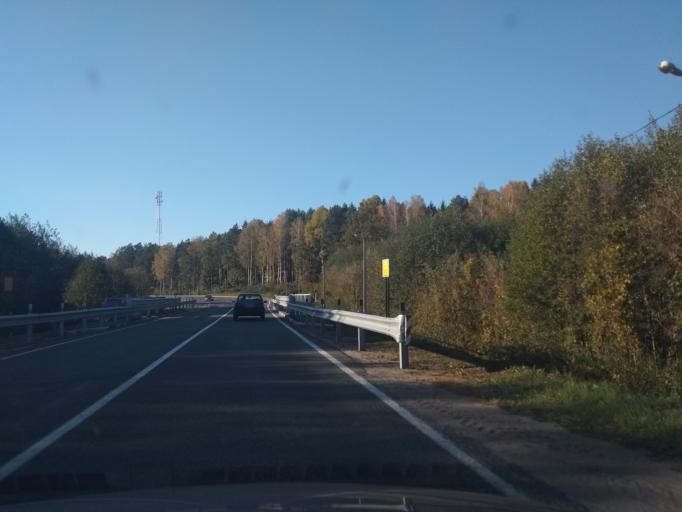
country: BY
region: Grodnenskaya
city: Vyalikaya Byerastavitsa
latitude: 53.1195
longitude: 23.9206
